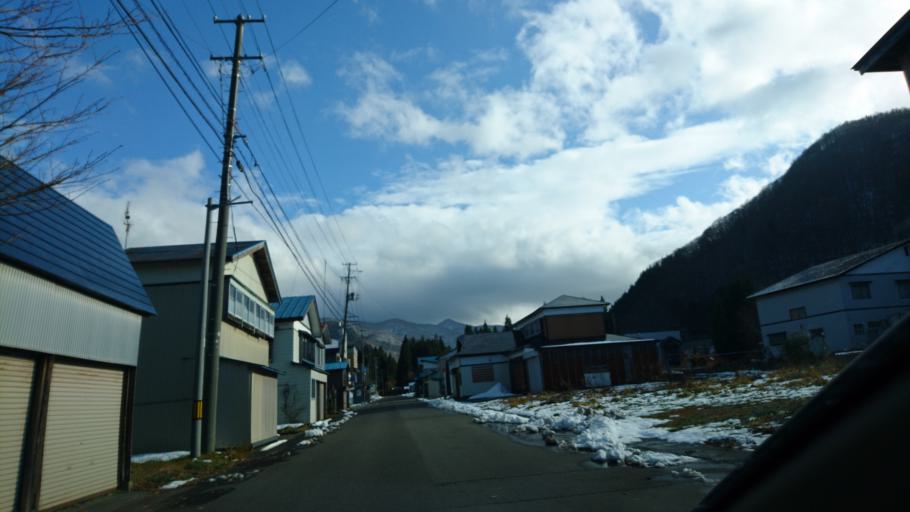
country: JP
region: Iwate
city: Kitakami
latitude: 39.2964
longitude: 140.8354
